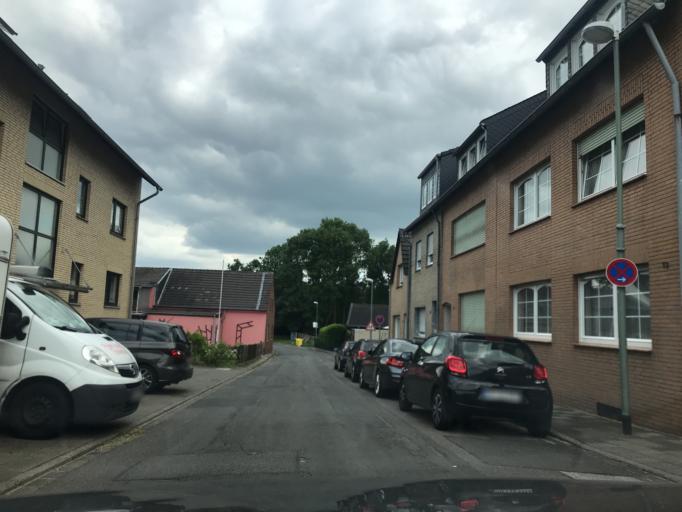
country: DE
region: North Rhine-Westphalia
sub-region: Regierungsbezirk Dusseldorf
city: Neubrueck
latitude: 51.1567
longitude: 6.6710
